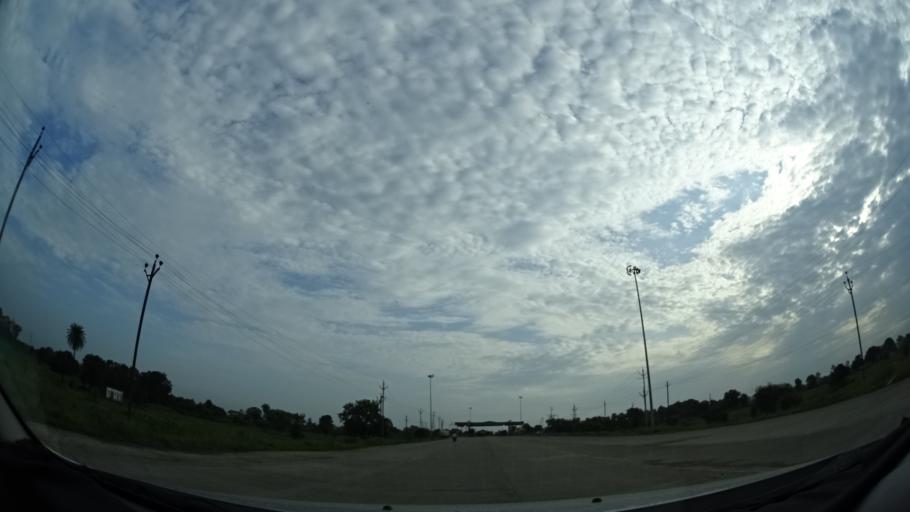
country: IN
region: Madhya Pradesh
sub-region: Bhopal
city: Bhopal
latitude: 23.3096
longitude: 77.3184
